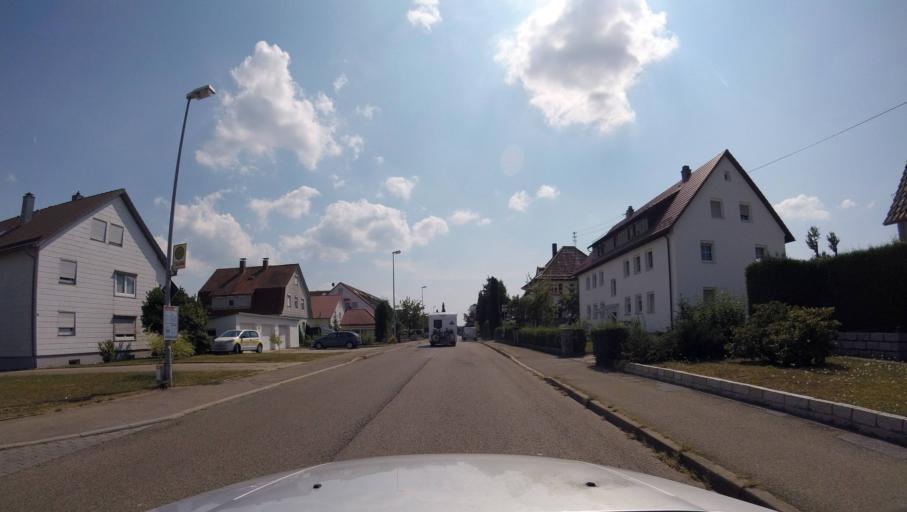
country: DE
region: Baden-Wuerttemberg
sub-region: Regierungsbezirk Stuttgart
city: Welzheim
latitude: 48.8821
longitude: 9.6332
